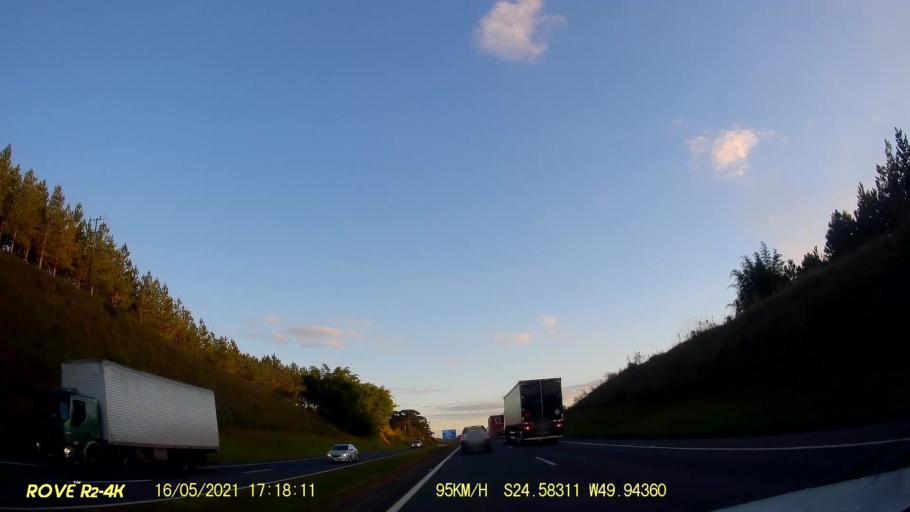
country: BR
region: Parana
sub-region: Pirai Do Sul
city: Pirai do Sul
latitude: -24.5833
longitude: -49.9437
